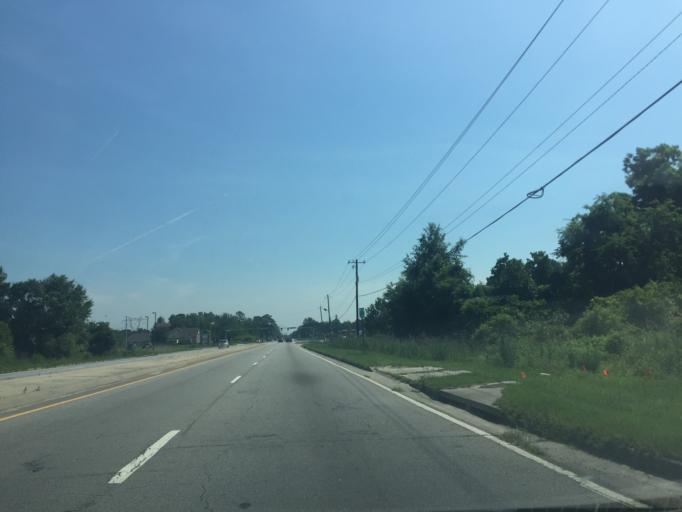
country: US
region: Georgia
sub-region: Bryan County
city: Richmond Hill
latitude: 31.9515
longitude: -81.3110
